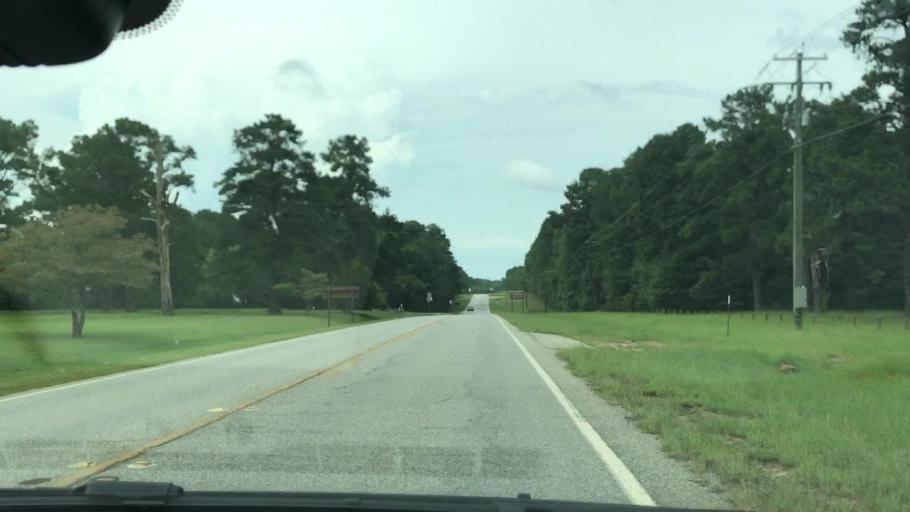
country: US
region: Georgia
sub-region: Clay County
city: Fort Gaines
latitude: 31.6359
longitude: -85.0441
